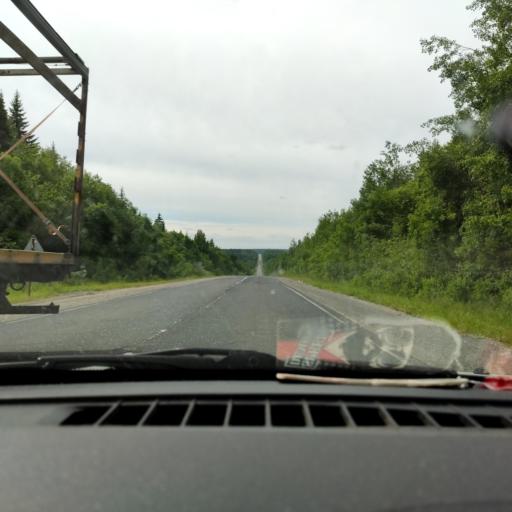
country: RU
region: Perm
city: Chusovoy
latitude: 58.3722
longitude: 58.0054
